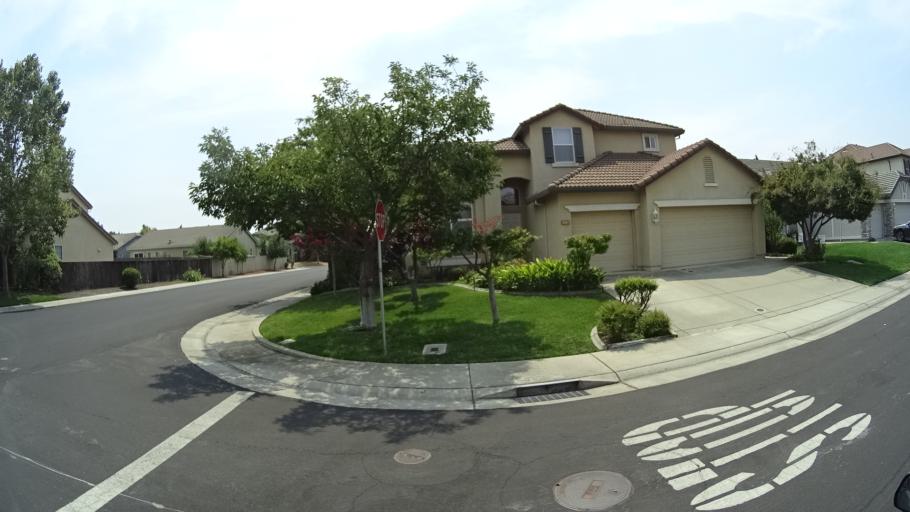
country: US
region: California
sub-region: Sacramento County
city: Laguna
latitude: 38.3849
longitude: -121.4304
